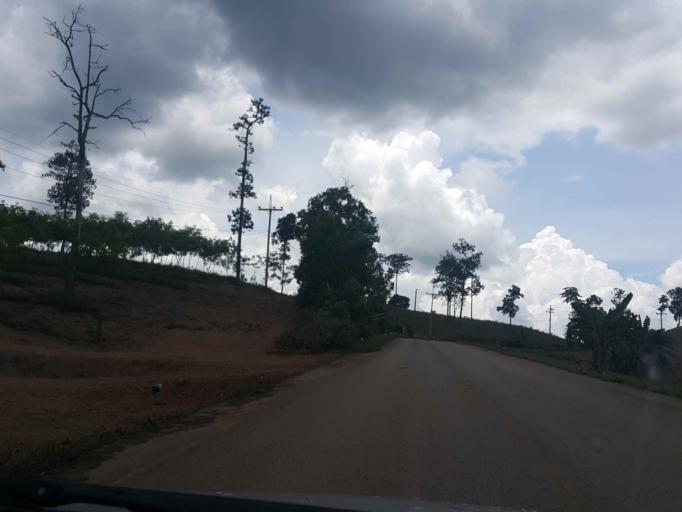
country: TH
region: Lampang
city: Ngao
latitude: 18.9489
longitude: 100.0777
